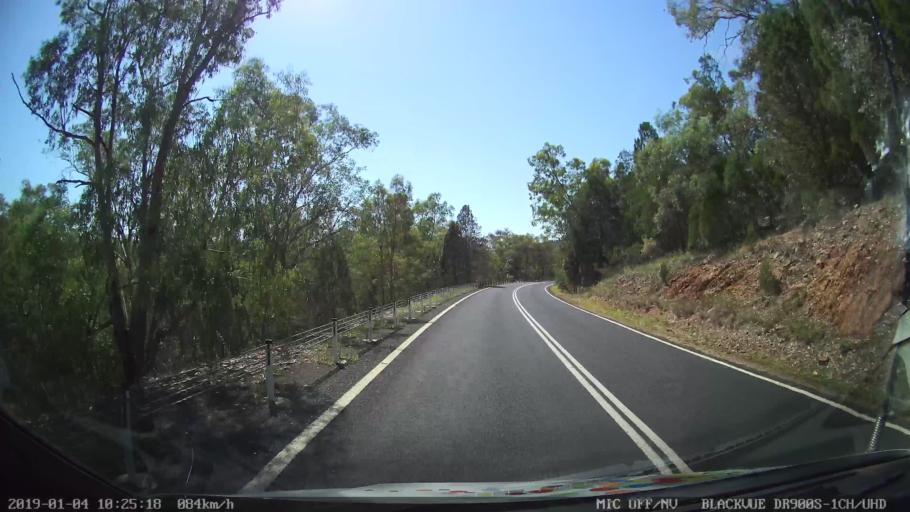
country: AU
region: New South Wales
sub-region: Cabonne
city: Canowindra
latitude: -33.3680
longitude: 148.5684
